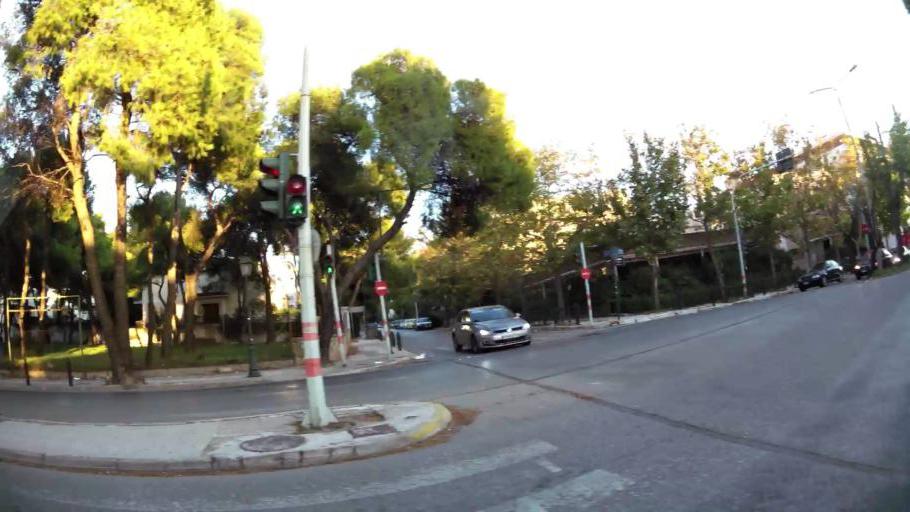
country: GR
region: Attica
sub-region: Nomarchia Athinas
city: Kifisia
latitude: 38.0752
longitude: 23.8211
